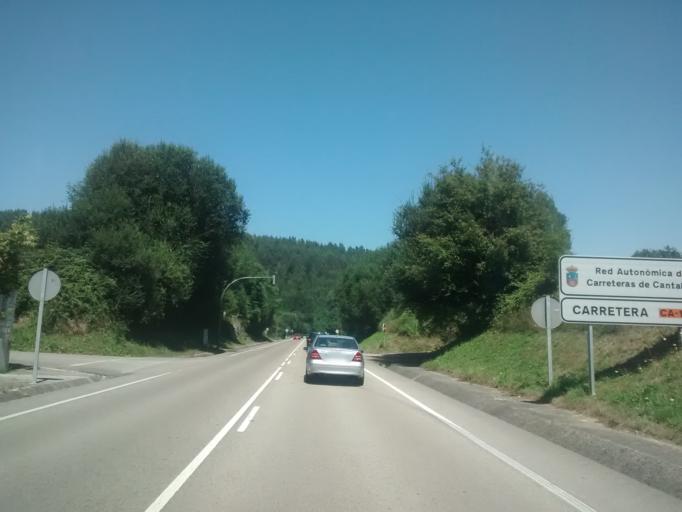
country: ES
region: Cantabria
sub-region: Provincia de Cantabria
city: Hazas de Cesto
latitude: 43.4235
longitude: -3.5688
